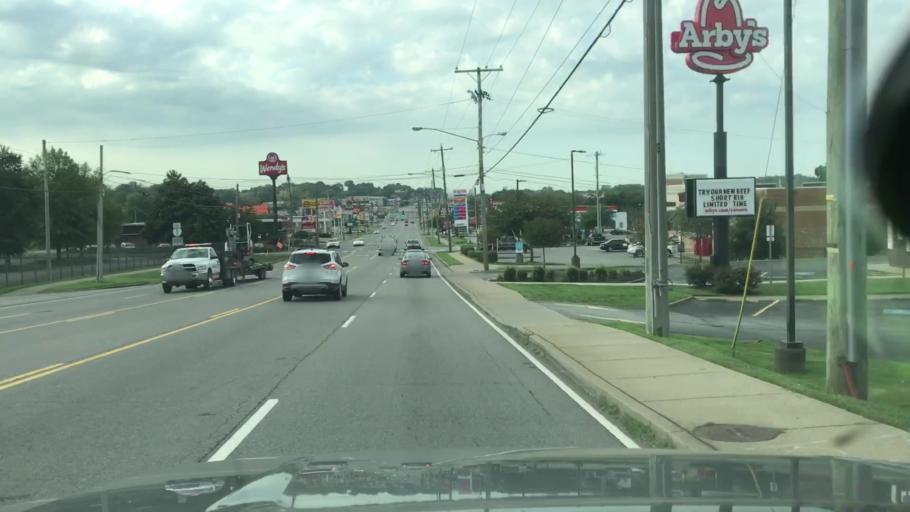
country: US
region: Tennessee
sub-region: Davidson County
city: Nashville
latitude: 36.2343
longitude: -86.7585
